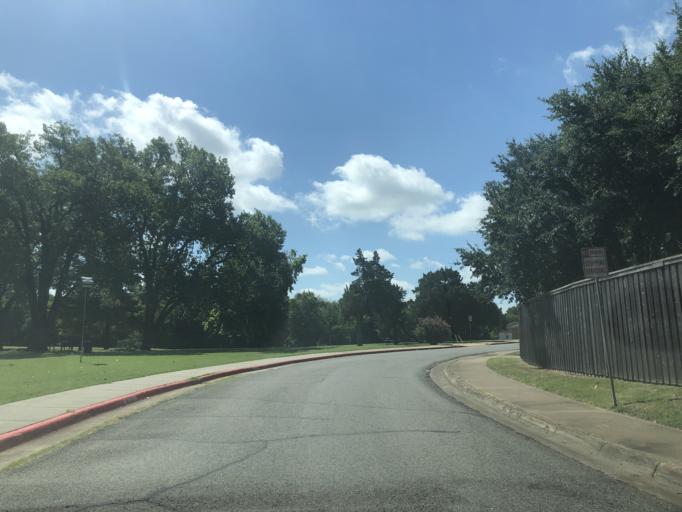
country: US
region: Texas
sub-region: Dallas County
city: Duncanville
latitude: 32.6554
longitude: -96.9217
